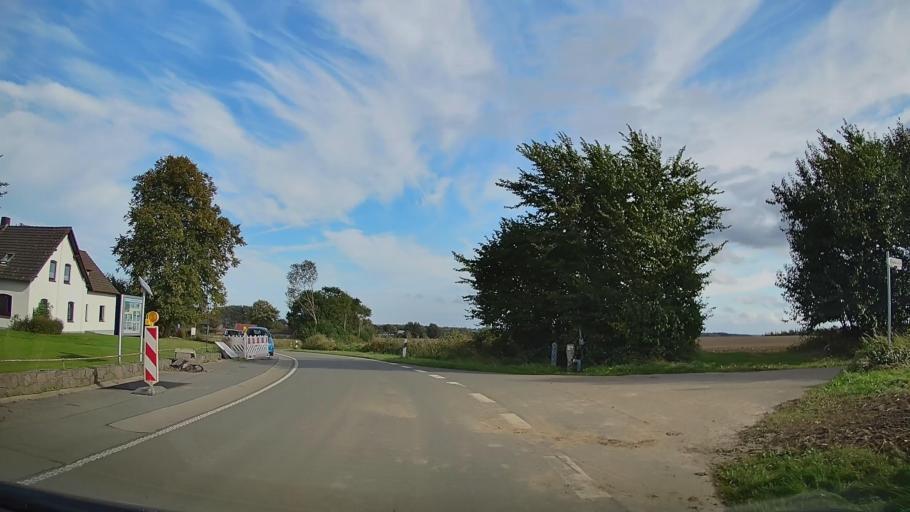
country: DE
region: Schleswig-Holstein
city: Steinbergkirche
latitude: 54.8011
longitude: 9.7444
